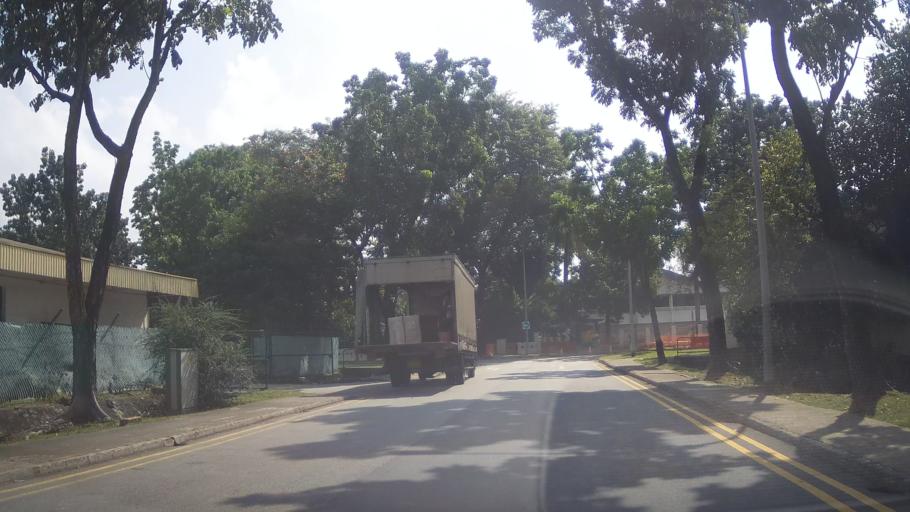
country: MY
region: Johor
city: Johor Bahru
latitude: 1.3264
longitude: 103.7025
